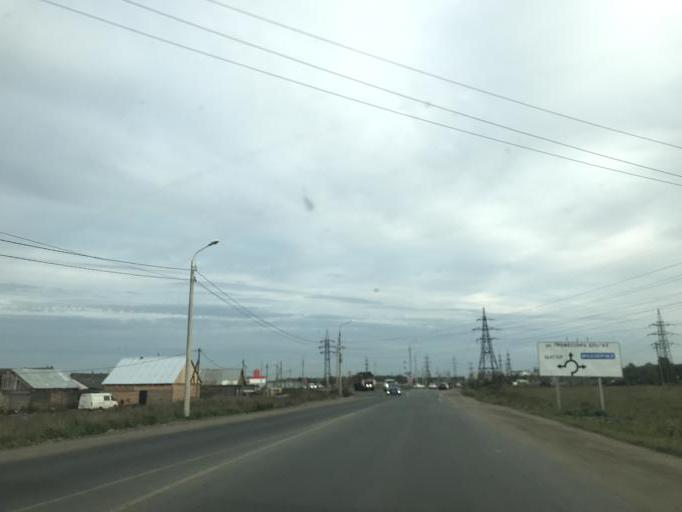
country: RU
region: Chelyabinsk
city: Roshchino
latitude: 55.2324
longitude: 61.2828
